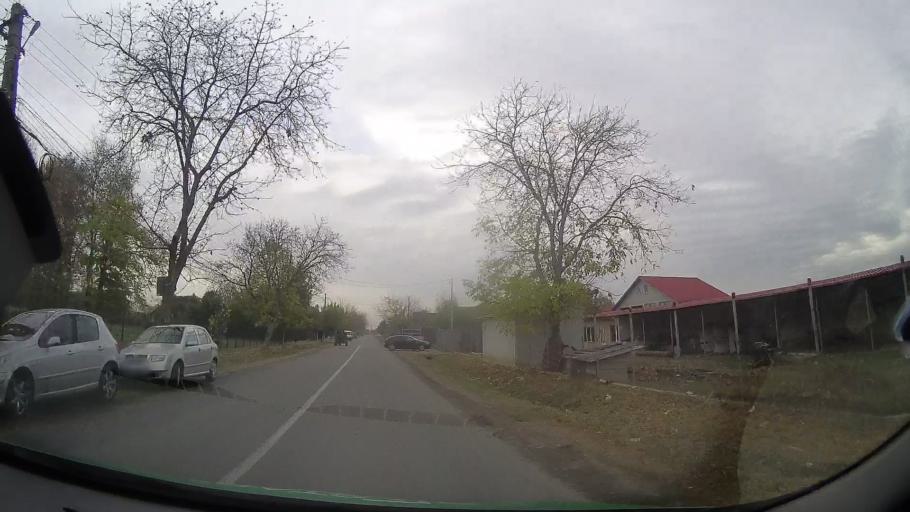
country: RO
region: Prahova
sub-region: Comuna Valea Calugareasca
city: Pantazi
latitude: 44.9161
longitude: 26.1568
